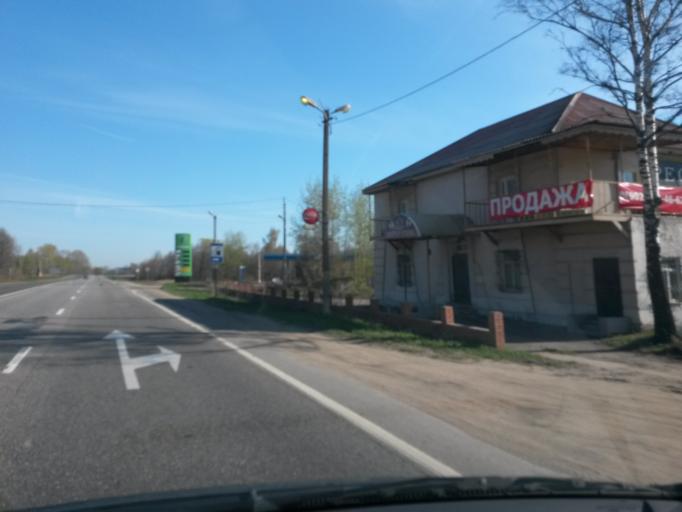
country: RU
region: Jaroslavl
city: Ishnya
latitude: 57.1697
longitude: 39.3581
